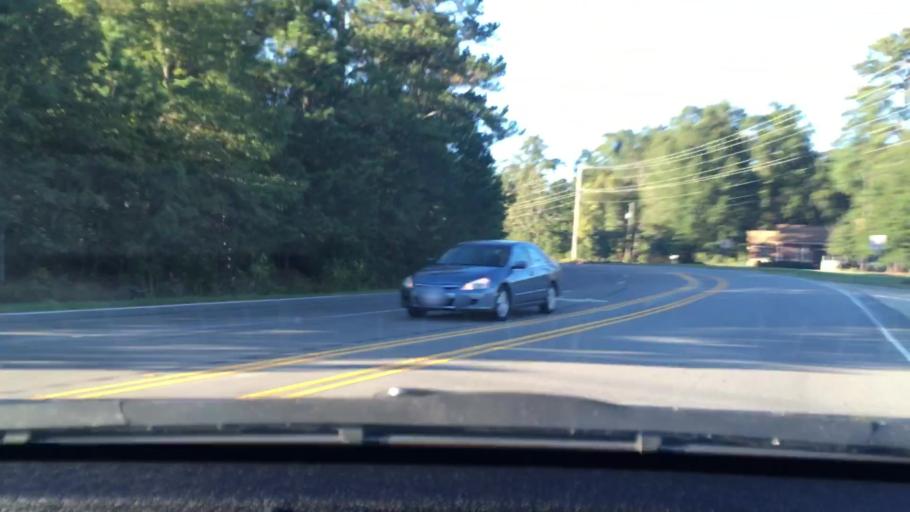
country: US
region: South Carolina
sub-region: Lexington County
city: Irmo
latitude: 34.0984
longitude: -81.1674
